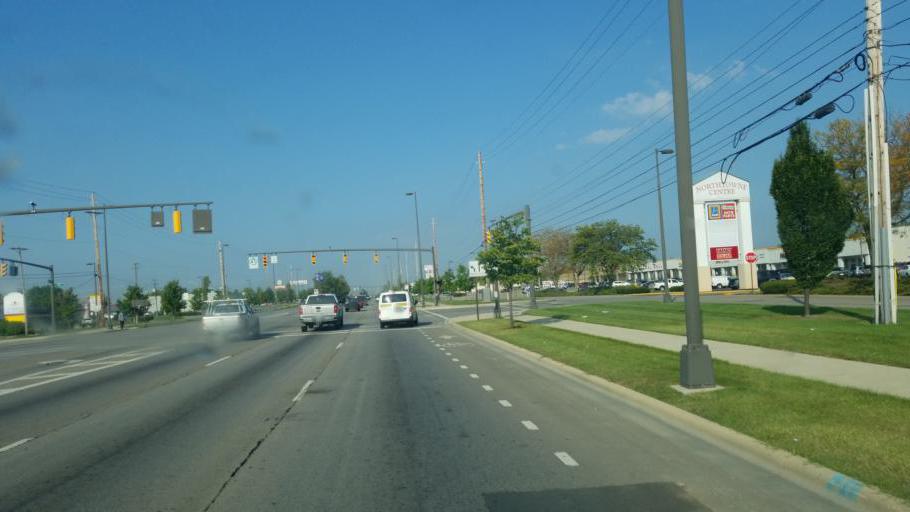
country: US
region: Ohio
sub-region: Franklin County
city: Minerva Park
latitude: 40.0599
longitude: -82.9571
